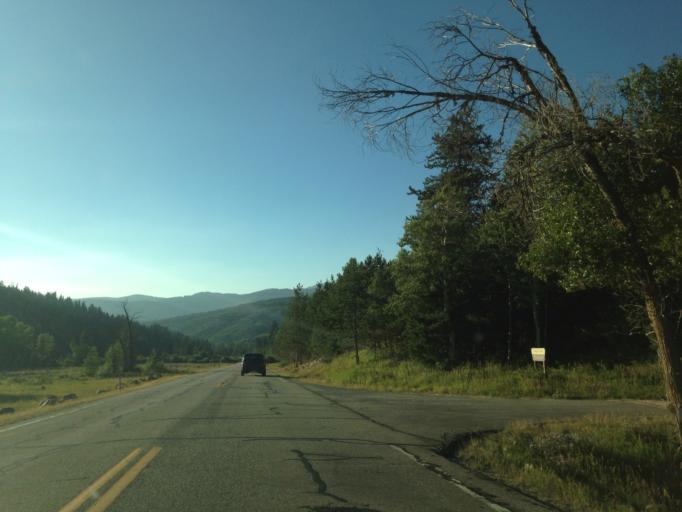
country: US
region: Utah
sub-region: Summit County
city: Francis
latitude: 40.6107
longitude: -111.1242
